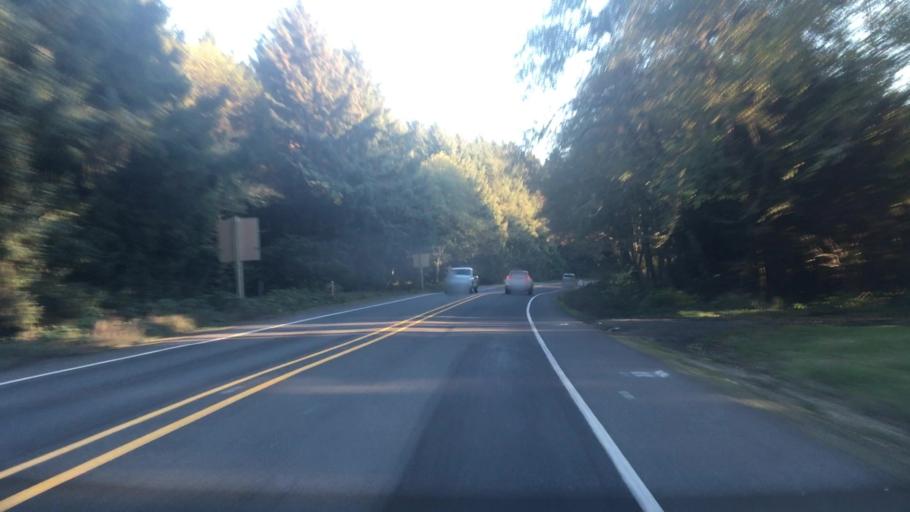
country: US
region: Oregon
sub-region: Clatsop County
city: Cannon Beach
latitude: 45.8803
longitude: -123.9580
